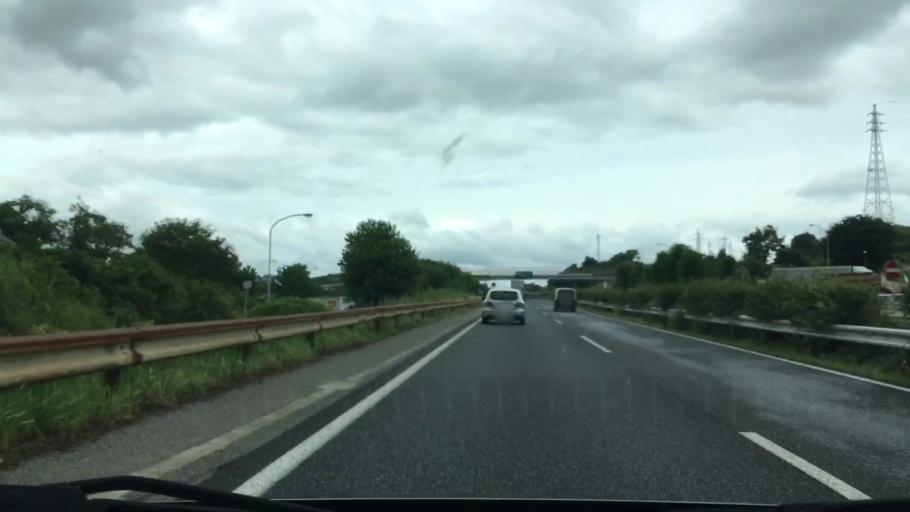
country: JP
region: Okayama
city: Tsuyama
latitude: 35.0641
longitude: 133.9749
